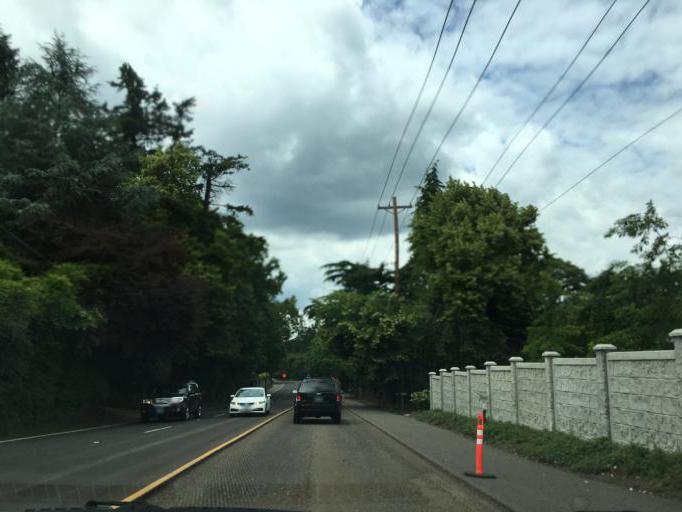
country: US
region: Oregon
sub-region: Clackamas County
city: Milwaukie
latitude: 45.4513
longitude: -122.6593
